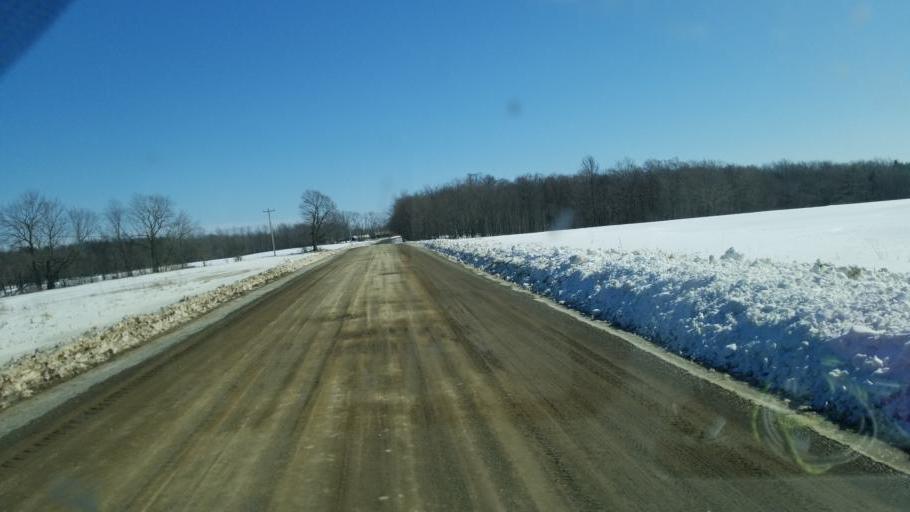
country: US
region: New York
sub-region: Allegany County
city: Andover
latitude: 42.0973
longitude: -77.6829
